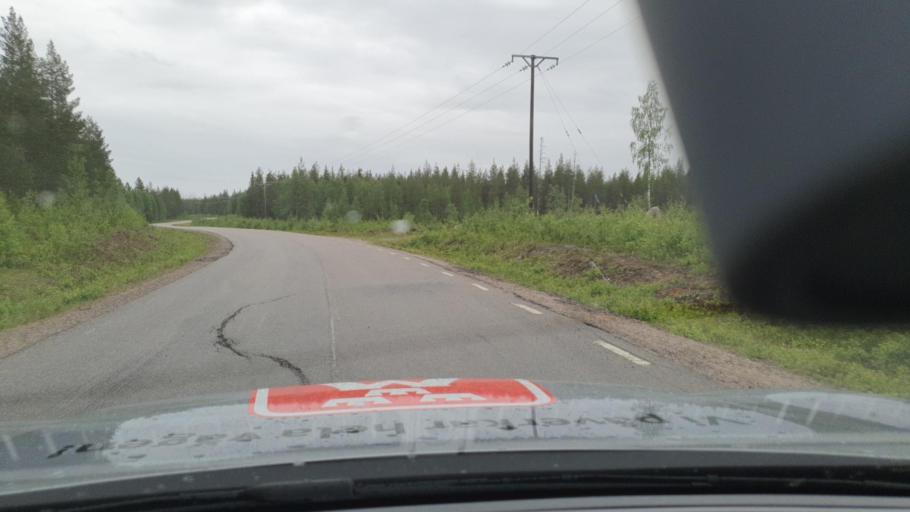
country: SE
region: Norrbotten
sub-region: Pajala Kommun
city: Pajala
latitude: 66.7708
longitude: 23.1459
